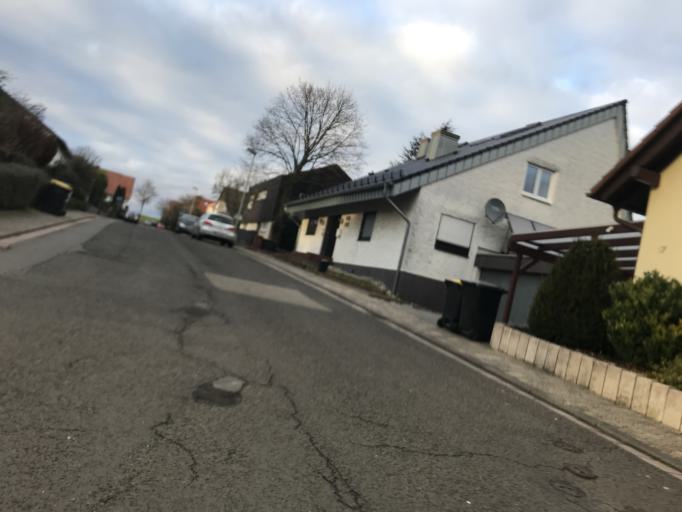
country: DE
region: Rheinland-Pfalz
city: Ober-Olm
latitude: 49.9411
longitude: 8.2001
